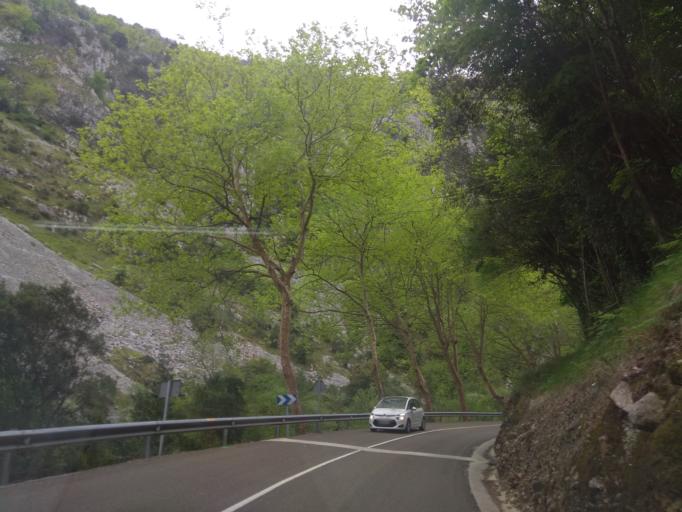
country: ES
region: Cantabria
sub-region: Provincia de Cantabria
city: Tresviso
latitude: 43.2893
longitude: -4.6192
